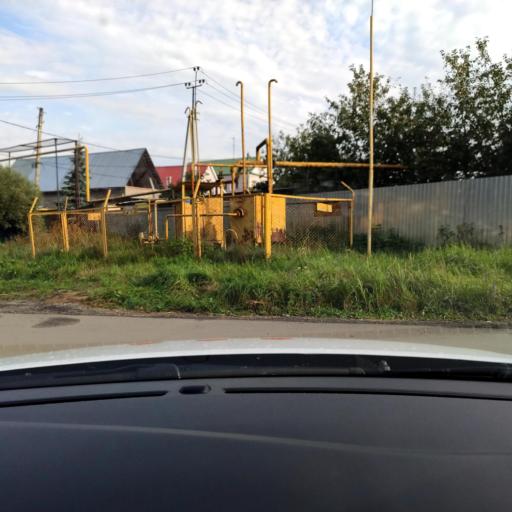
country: RU
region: Tatarstan
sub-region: Gorod Kazan'
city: Kazan
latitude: 55.9118
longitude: 49.1525
